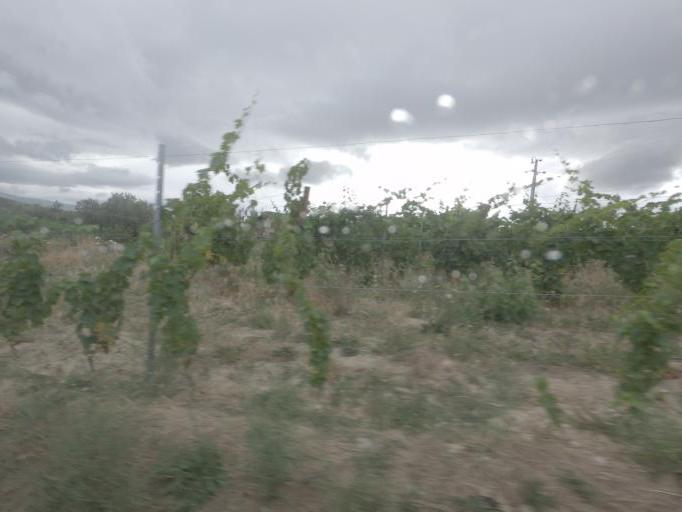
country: PT
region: Vila Real
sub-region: Sabrosa
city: Sabrosa
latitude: 41.2465
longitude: -7.4987
